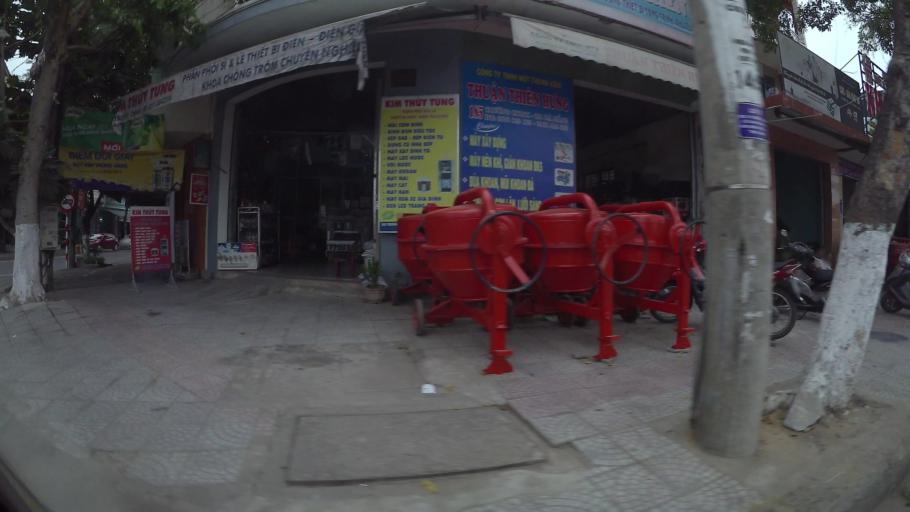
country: VN
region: Da Nang
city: Thanh Khe
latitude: 16.0566
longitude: 108.1807
